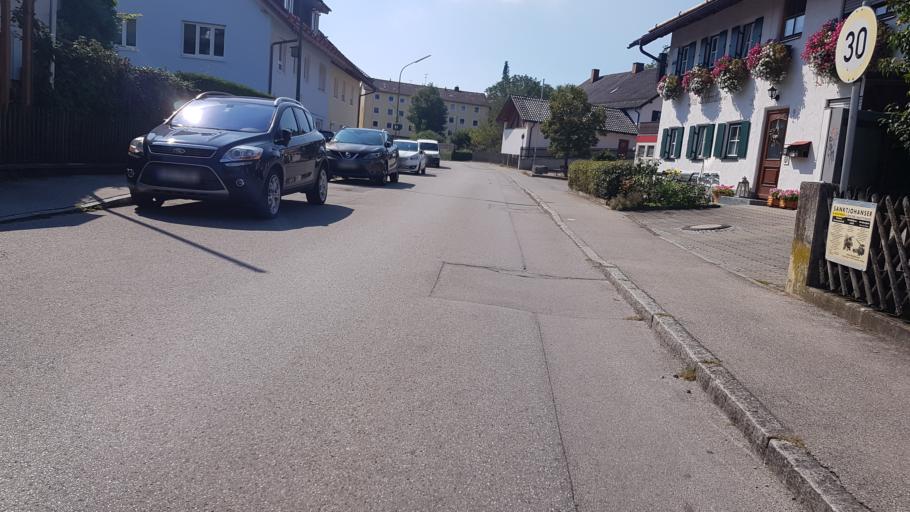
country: DE
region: Bavaria
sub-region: Upper Bavaria
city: Seefeld
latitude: 48.0404
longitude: 11.1925
